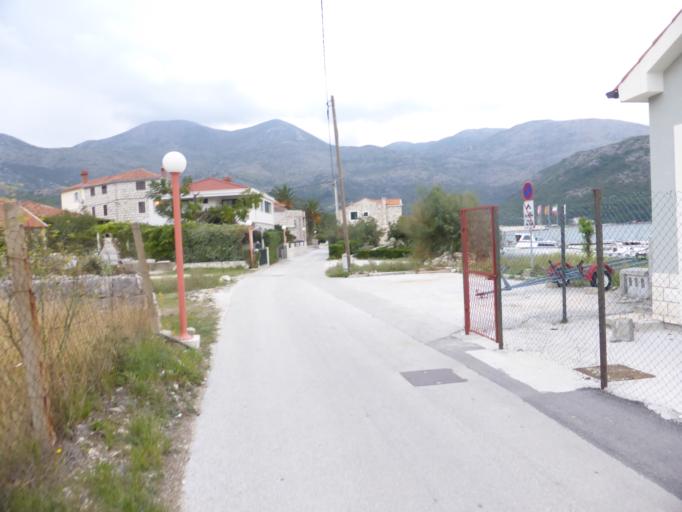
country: HR
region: Dubrovacko-Neretvanska
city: Podgora
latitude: 42.7831
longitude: 17.8764
